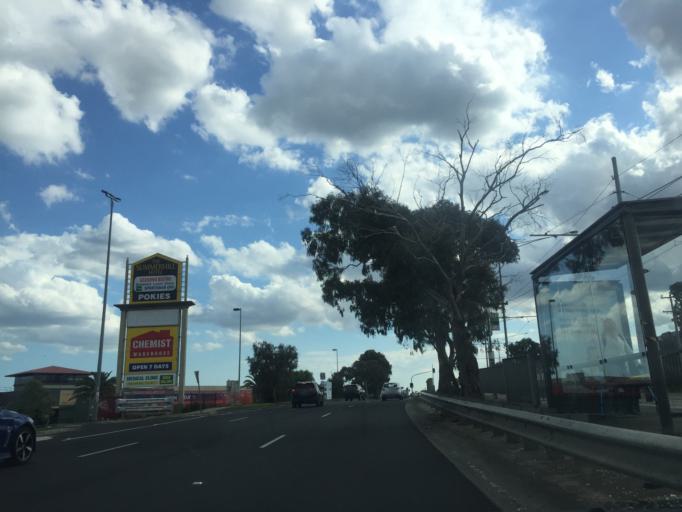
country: AU
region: Victoria
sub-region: Darebin
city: Kingsbury
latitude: -37.7245
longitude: 145.0274
